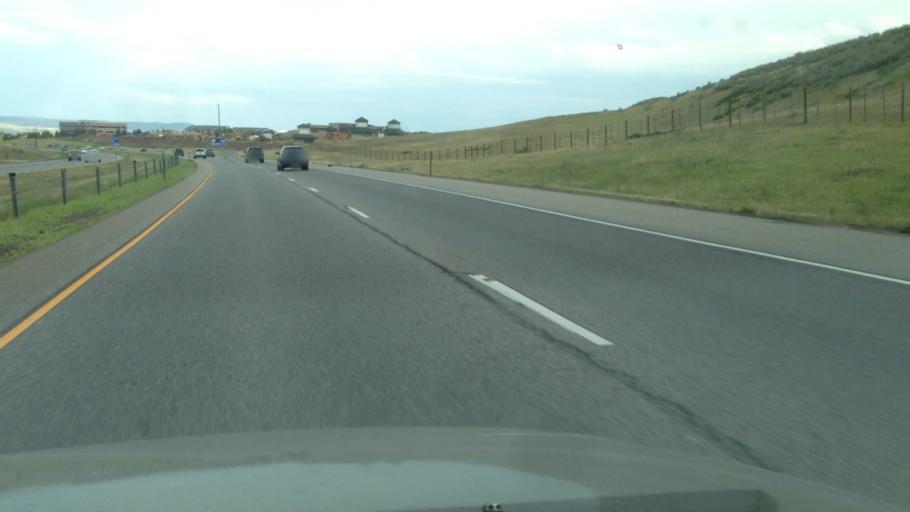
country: US
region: Colorado
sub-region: Jefferson County
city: Ken Caryl
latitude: 39.5642
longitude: -105.1279
